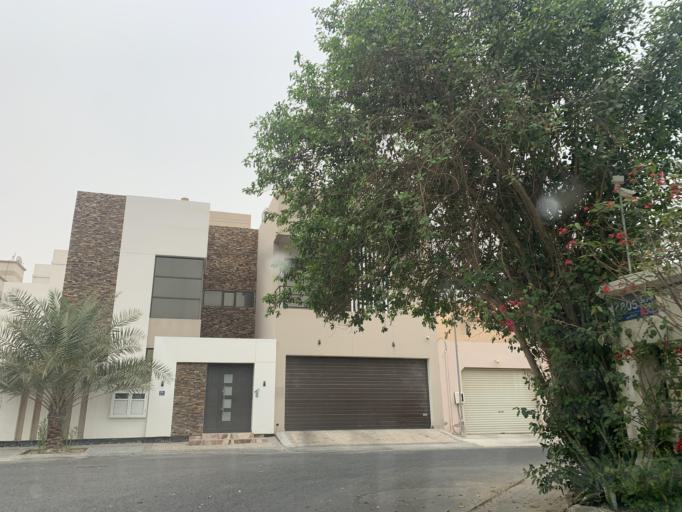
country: BH
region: Northern
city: Ar Rifa'
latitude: 26.1462
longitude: 50.5320
